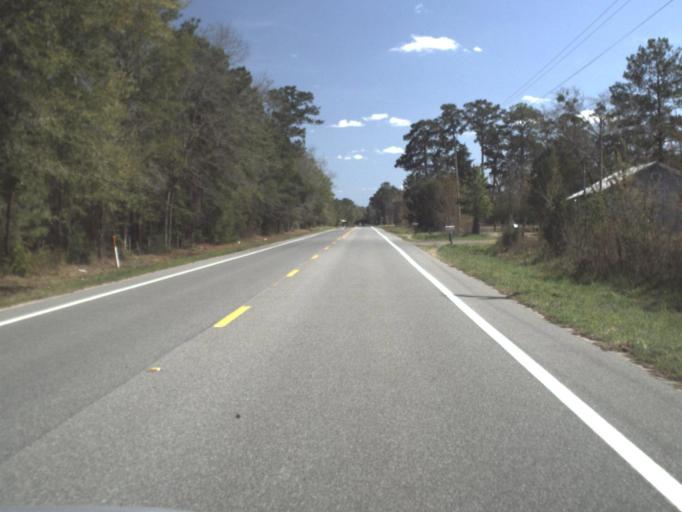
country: US
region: Florida
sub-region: Gadsden County
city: Gretna
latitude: 30.6665
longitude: -84.6980
